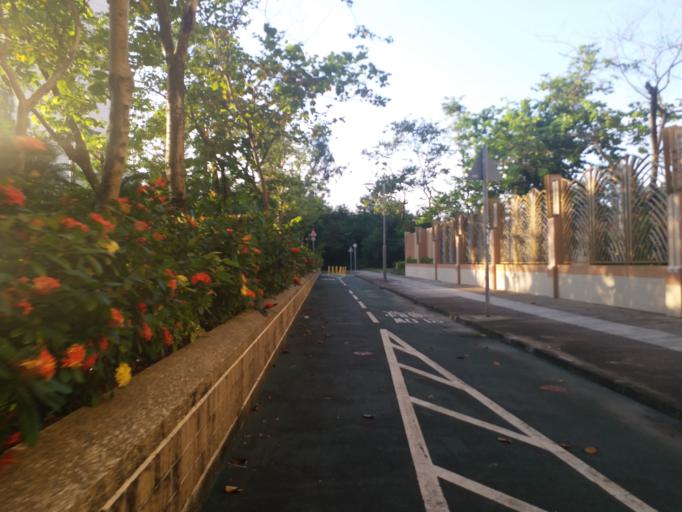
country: HK
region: Yuen Long
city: Yuen Long Kau Hui
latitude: 22.4508
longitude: 114.0320
